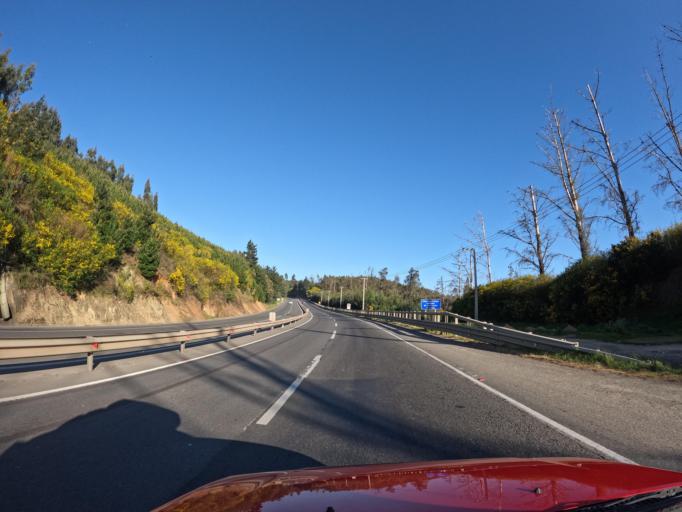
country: CL
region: Biobio
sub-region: Provincia de Concepcion
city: Penco
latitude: -36.7579
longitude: -72.9777
